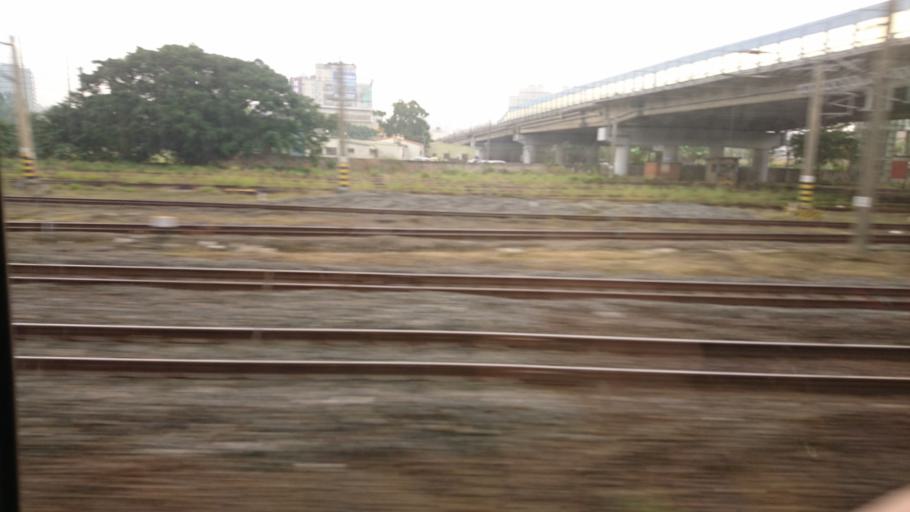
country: TW
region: Taiwan
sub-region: Hsinchu
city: Hsinchu
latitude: 24.8086
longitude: 120.9838
